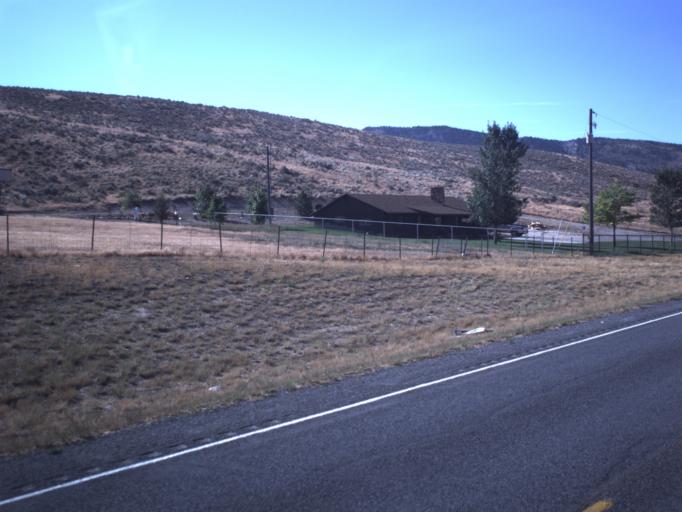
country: US
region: Utah
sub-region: Sanpete County
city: Manti
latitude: 39.2074
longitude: -111.6904
